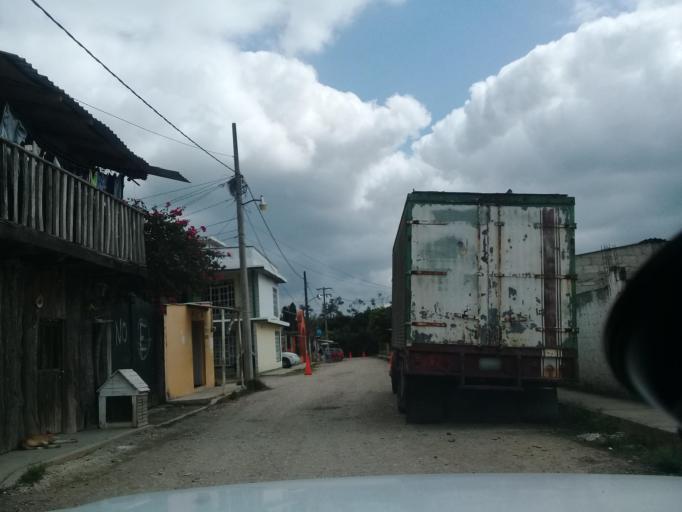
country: MX
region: Veracruz
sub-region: Xalapa
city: Fraccionamiento las Fuentes
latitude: 19.4737
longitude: -96.8796
